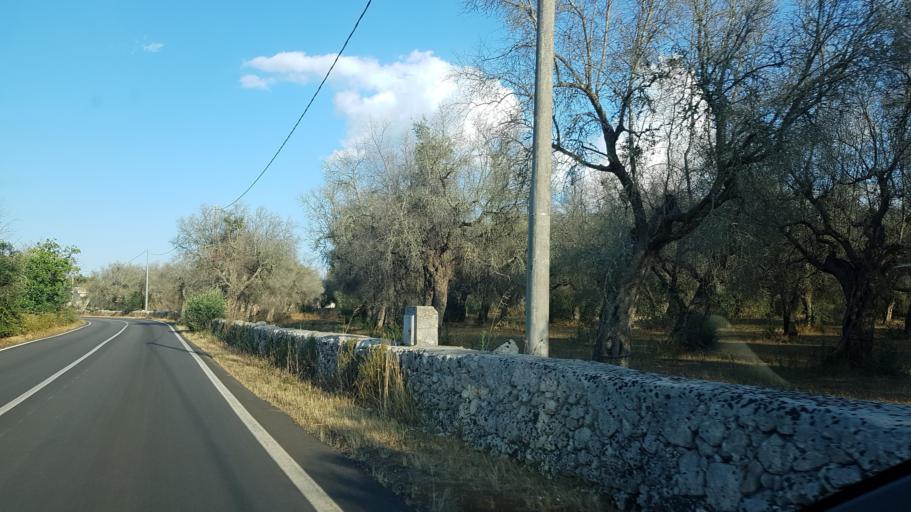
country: IT
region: Apulia
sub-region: Provincia di Lecce
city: Andrano
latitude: 39.9820
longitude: 18.3687
